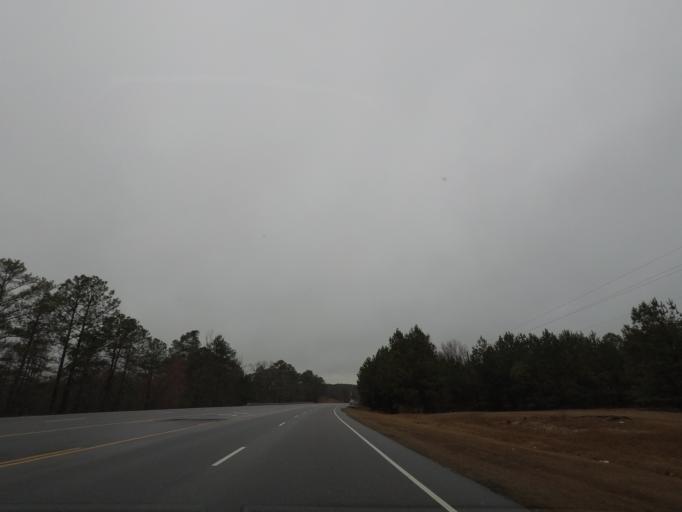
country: US
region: North Carolina
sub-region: Lee County
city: Broadway
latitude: 35.3442
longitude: -79.1055
